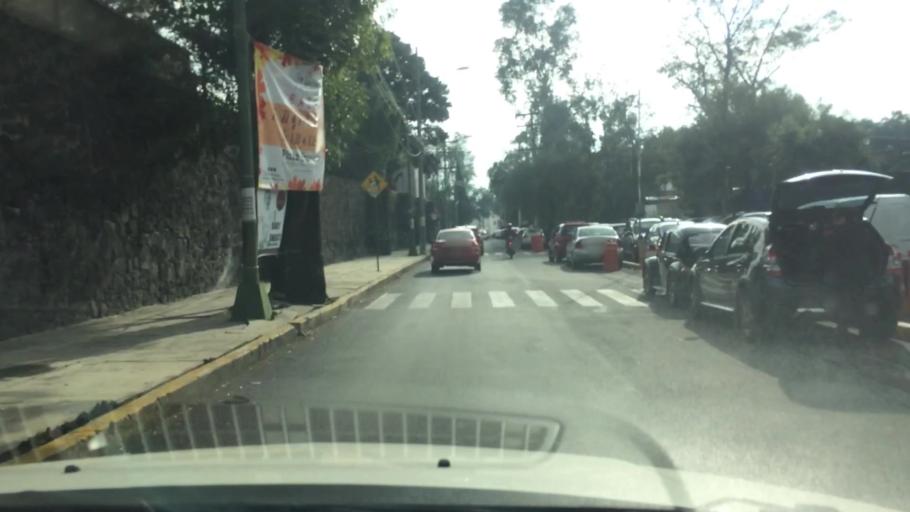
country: MX
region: Mexico City
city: Magdalena Contreras
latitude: 19.3097
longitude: -99.2117
